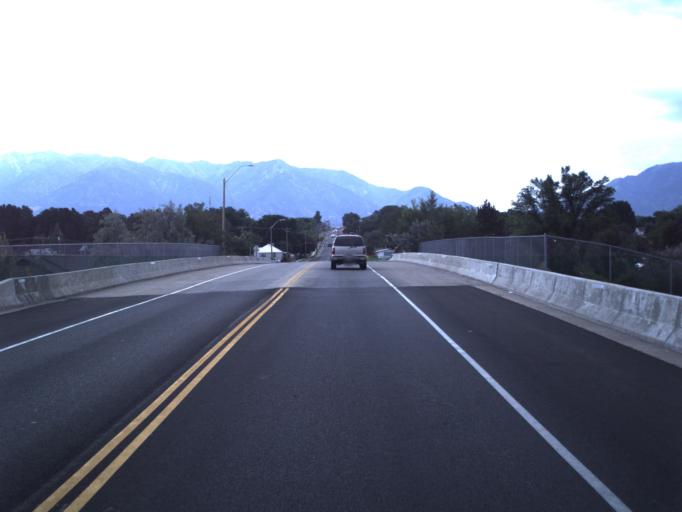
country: US
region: Utah
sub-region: Weber County
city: Roy
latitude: 41.1617
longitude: -112.0416
